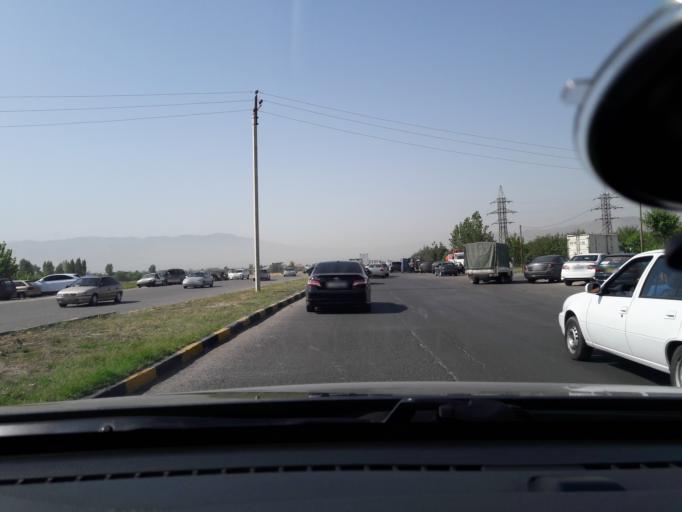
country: TJ
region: Dushanbe
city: Dushanbe
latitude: 38.4994
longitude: 68.7555
